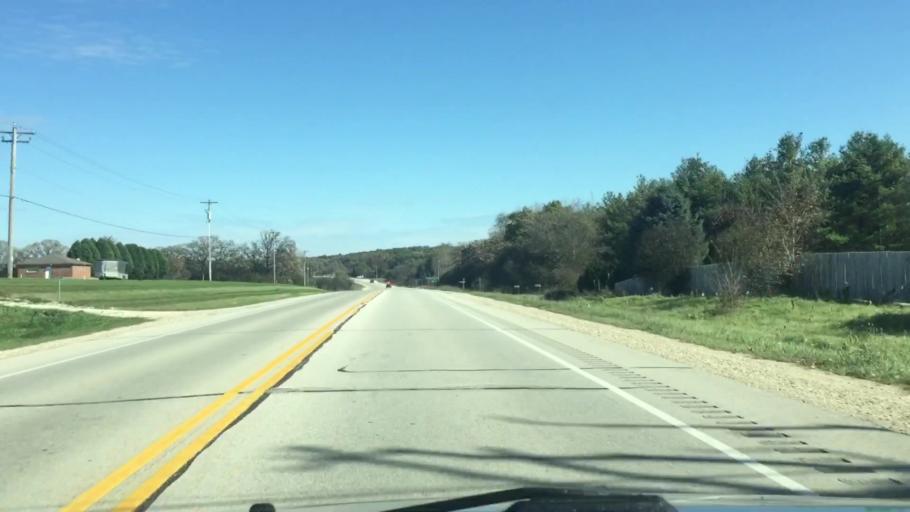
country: US
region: Wisconsin
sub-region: Waukesha County
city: Wales
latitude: 42.9618
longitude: -88.3288
